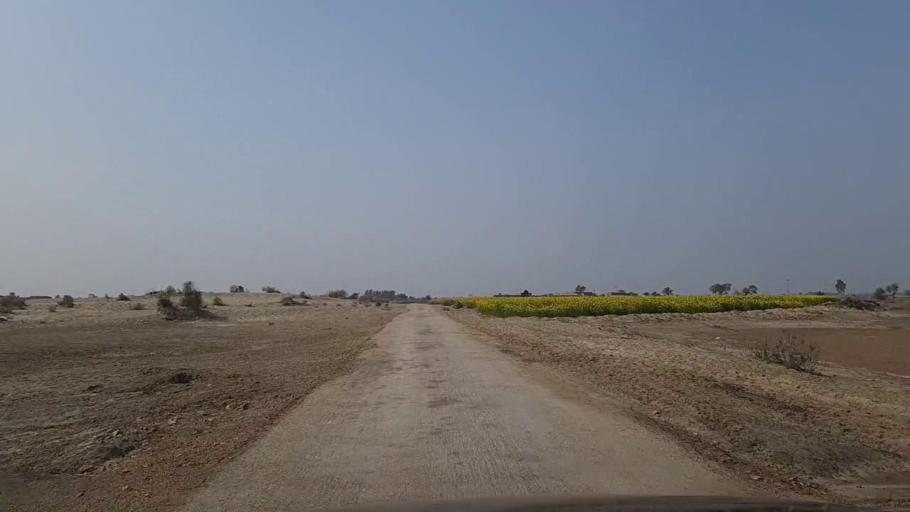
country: PK
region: Sindh
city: Daur
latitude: 26.3857
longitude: 68.4170
